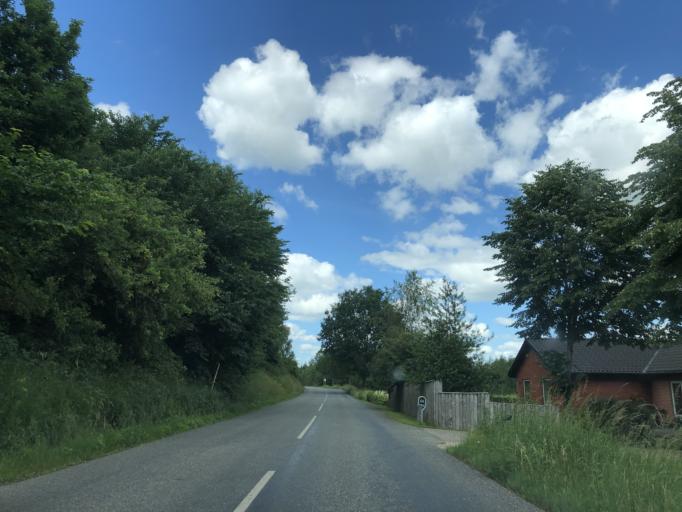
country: DK
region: Central Jutland
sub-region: Silkeborg Kommune
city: Svejbaek
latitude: 56.2293
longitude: 9.6656
